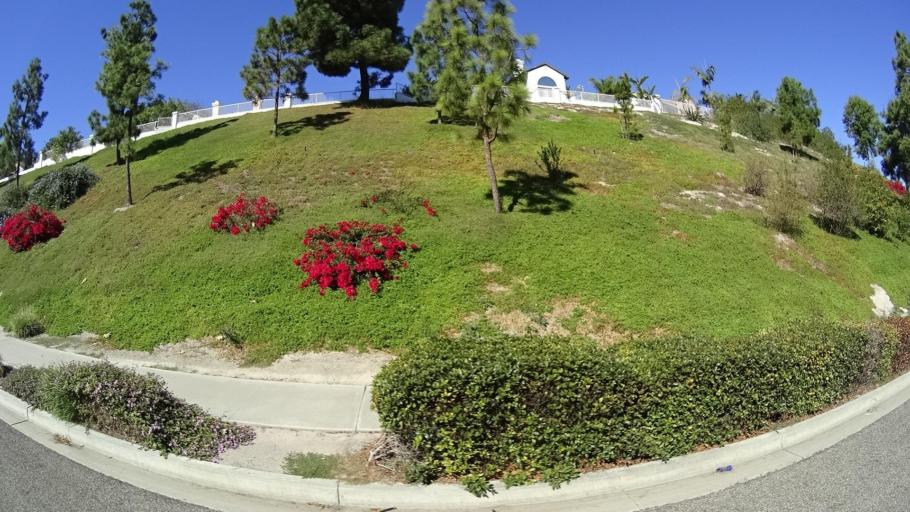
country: US
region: California
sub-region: San Diego County
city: Bonita
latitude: 32.6568
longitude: -116.9792
